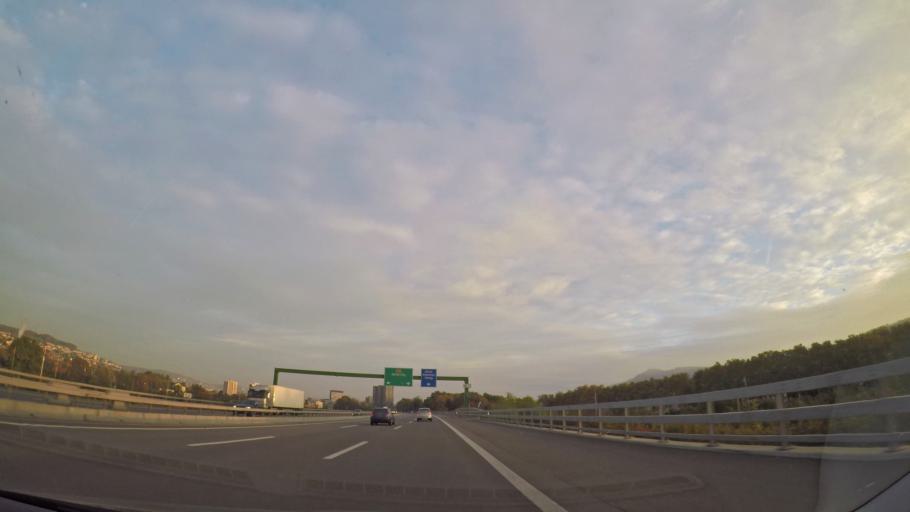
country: CH
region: Zurich
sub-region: Bezirk Dietikon
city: Oberengstringen
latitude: 47.4005
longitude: 8.4728
